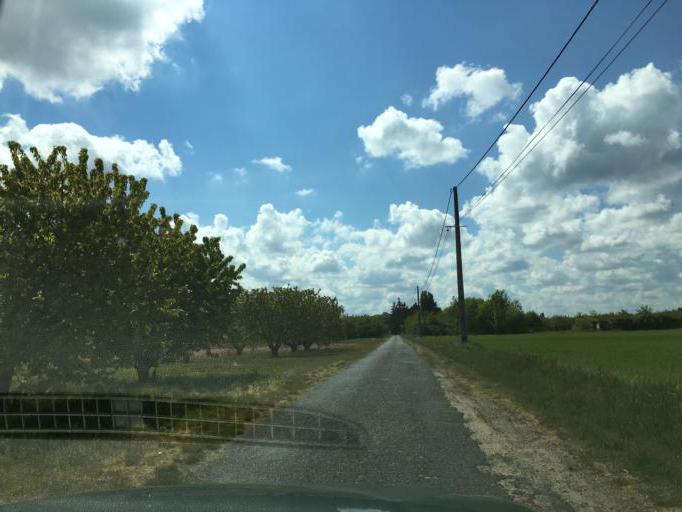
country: FR
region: Centre
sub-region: Departement du Loiret
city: Saint-Pryve-Saint-Mesmin
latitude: 47.8653
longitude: 1.8591
